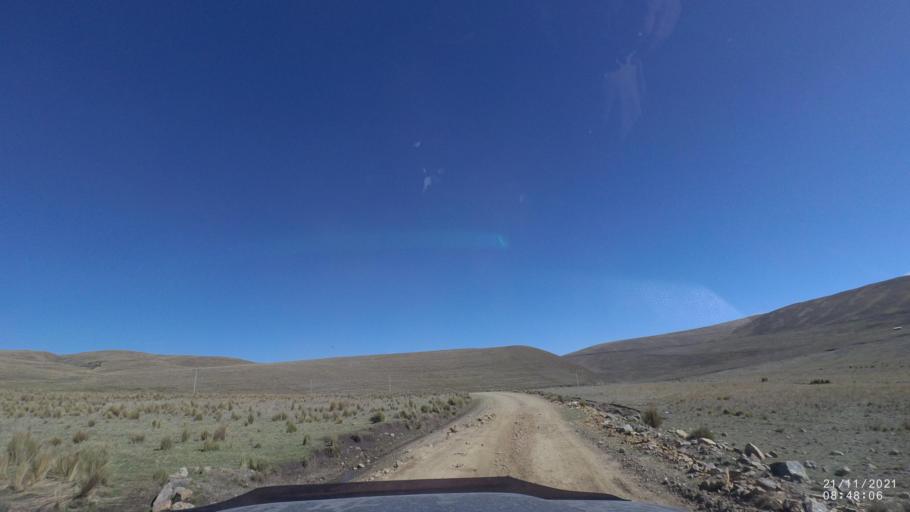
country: BO
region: Cochabamba
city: Cochabamba
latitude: -17.2317
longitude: -66.2331
